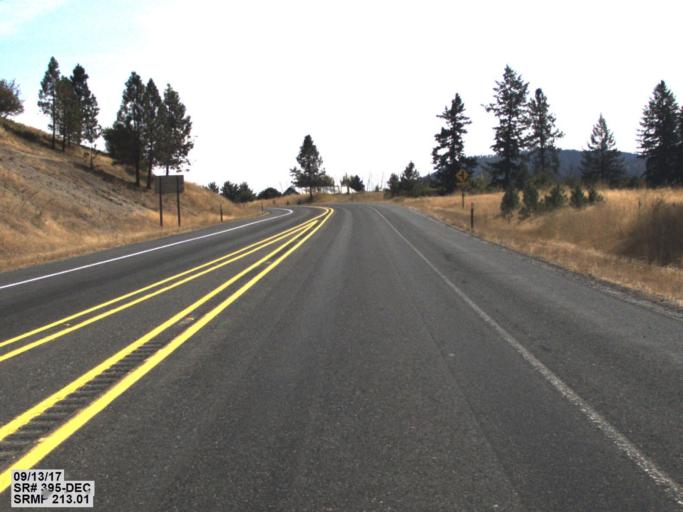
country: US
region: Washington
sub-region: Stevens County
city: Chewelah
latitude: 48.3191
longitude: -117.8179
